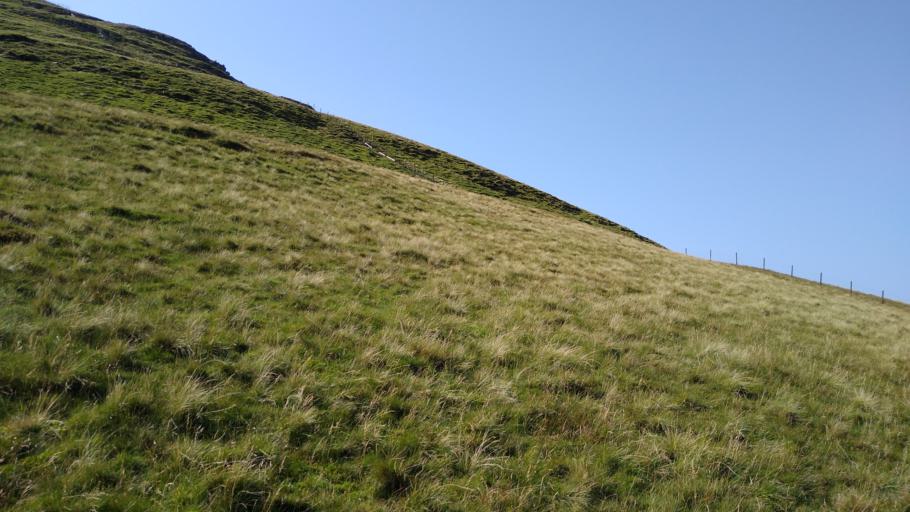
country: GB
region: England
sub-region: Cumbria
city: Cockermouth
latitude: 54.5416
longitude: -3.3598
